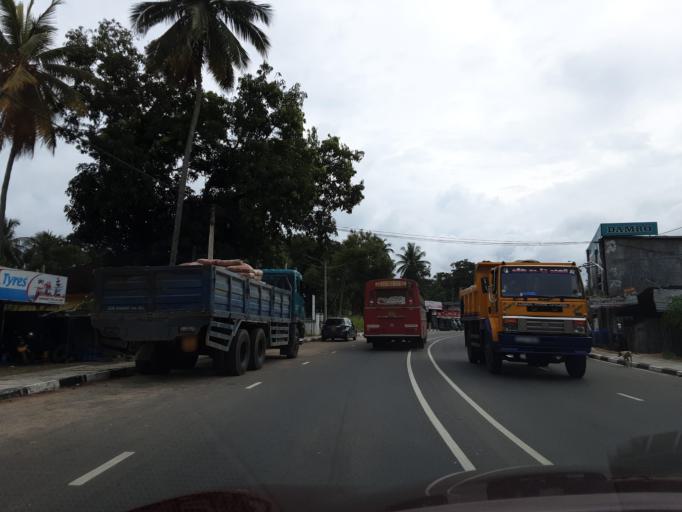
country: LK
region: Eastern Province
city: Ampara
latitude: 7.4008
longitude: 81.2432
